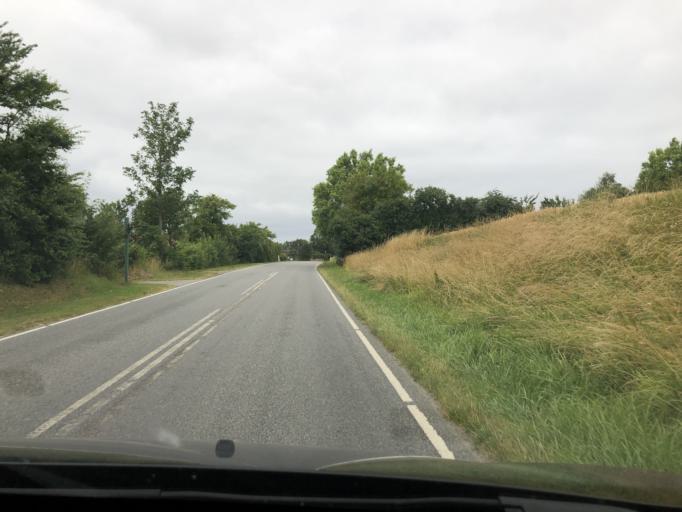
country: DK
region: South Denmark
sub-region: AEro Kommune
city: AEroskobing
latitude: 54.9273
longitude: 10.2699
